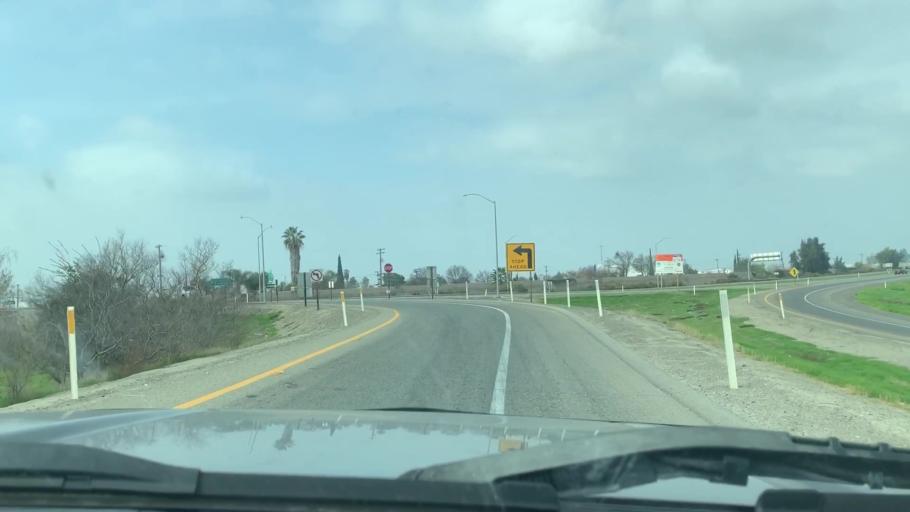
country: US
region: California
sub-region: Kings County
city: Lemoore
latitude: 36.2843
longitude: -119.8074
